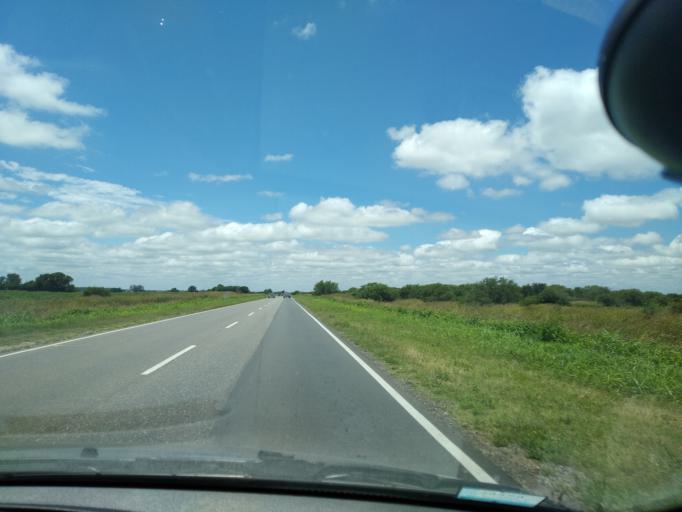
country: AR
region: Cordoba
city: Despenaderos
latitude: -31.6517
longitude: -64.2036
